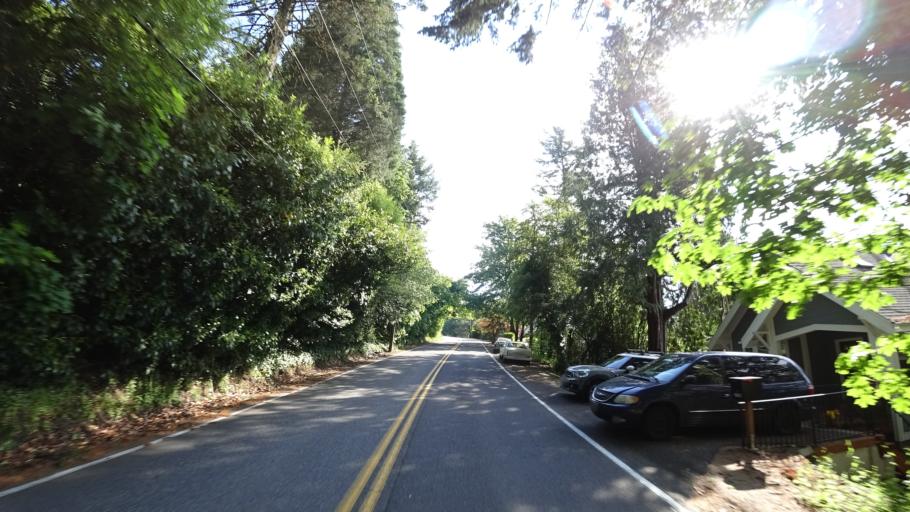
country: US
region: Oregon
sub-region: Multnomah County
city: Portland
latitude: 45.5005
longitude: -122.7158
